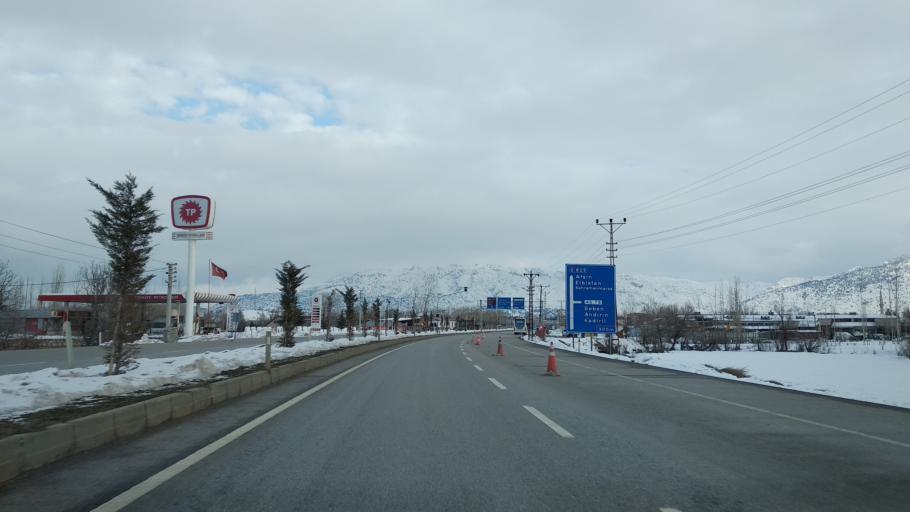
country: TR
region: Kahramanmaras
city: Goksun
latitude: 38.0309
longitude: 36.4768
